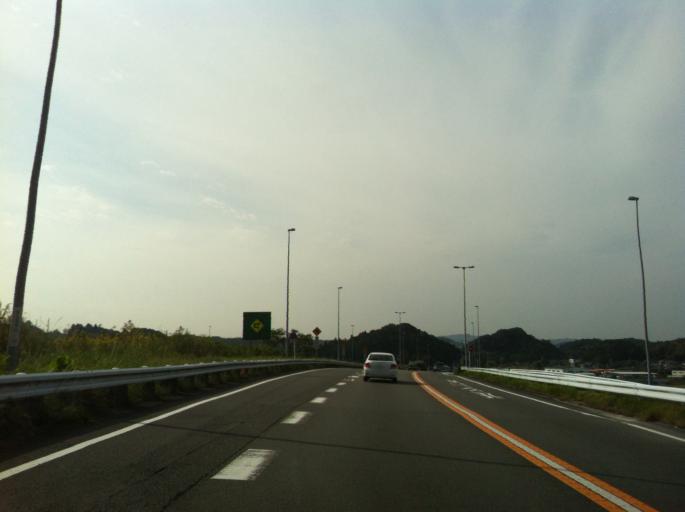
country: JP
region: Shizuoka
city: Kanaya
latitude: 34.7942
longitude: 138.0773
